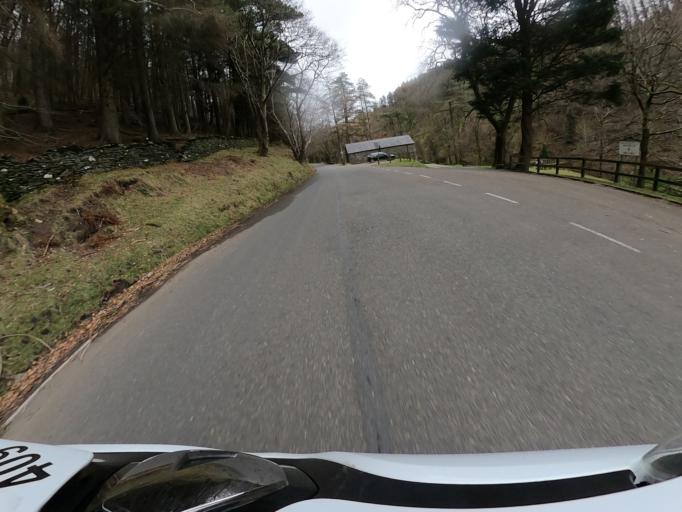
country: IM
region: Laxey
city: Laxey
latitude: 54.2771
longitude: -4.4920
